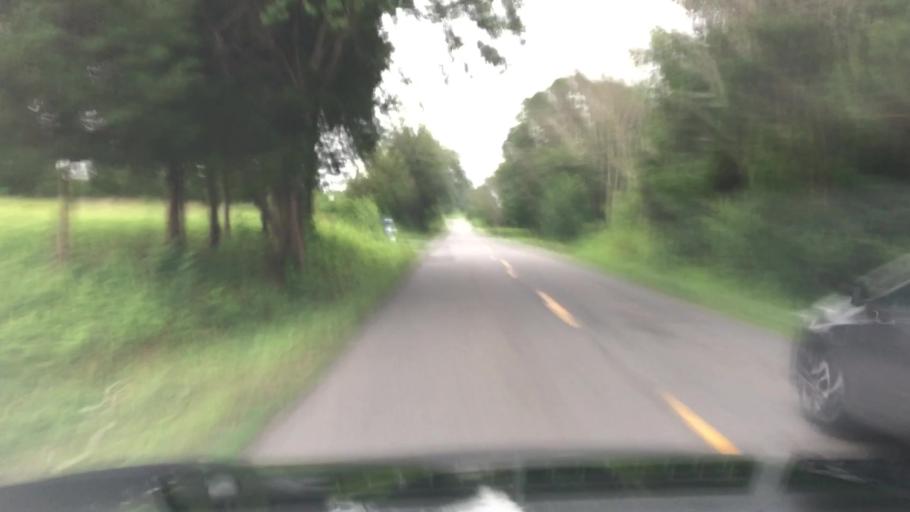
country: US
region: Virginia
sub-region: Prince William County
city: Nokesville
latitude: 38.6766
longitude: -77.6617
